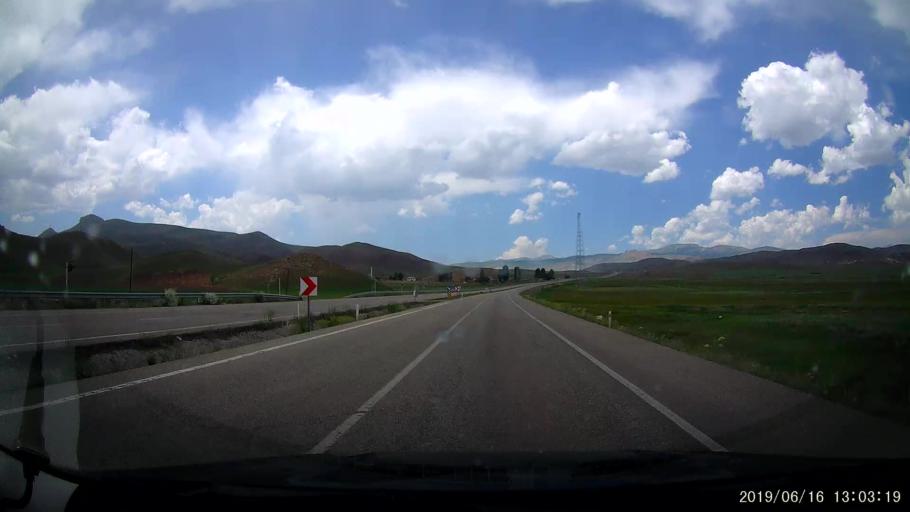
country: TR
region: Agri
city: Sulucem
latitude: 39.5802
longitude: 43.7930
